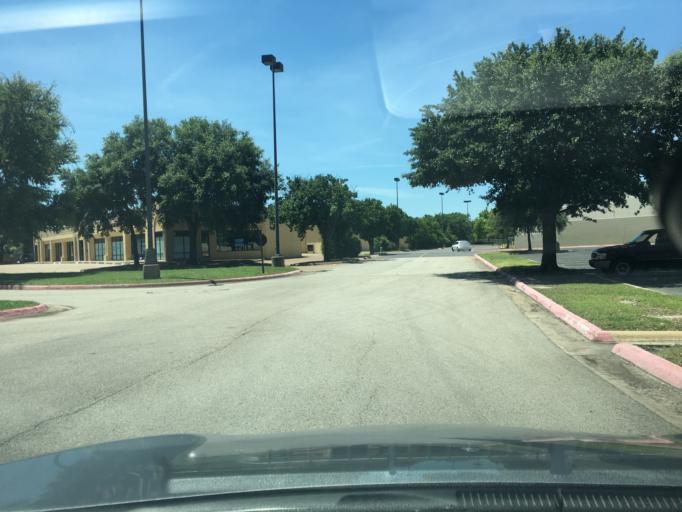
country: US
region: Texas
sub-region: Dallas County
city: Richardson
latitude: 32.9399
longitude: -96.6953
